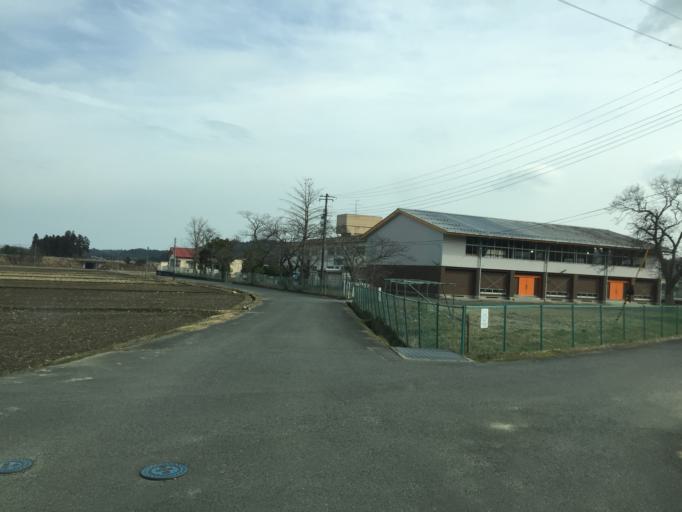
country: JP
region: Ibaraki
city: Kitaibaraki
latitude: 36.8865
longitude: 140.7410
